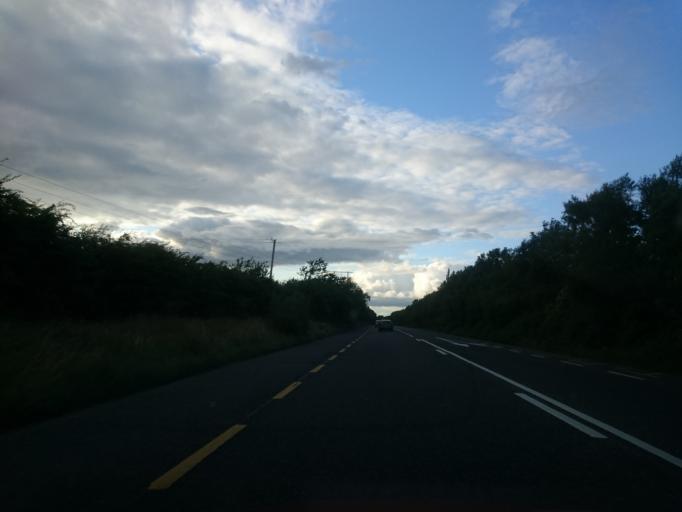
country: IE
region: Leinster
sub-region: Loch Garman
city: Castlebridge
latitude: 52.4047
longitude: -6.5203
